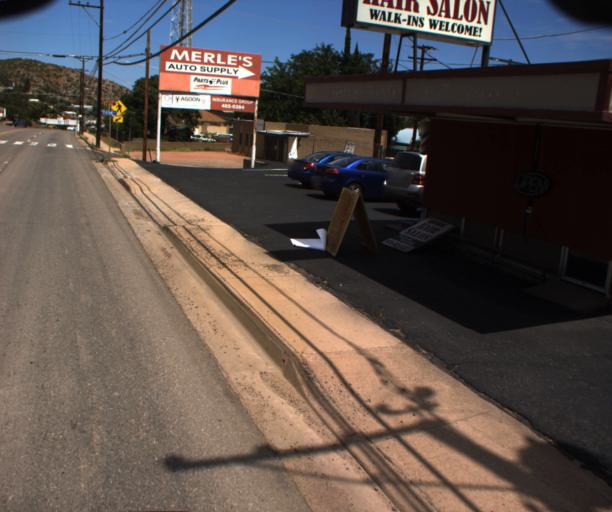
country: US
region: Arizona
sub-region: Gila County
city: Globe
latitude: 33.3991
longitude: -110.7905
